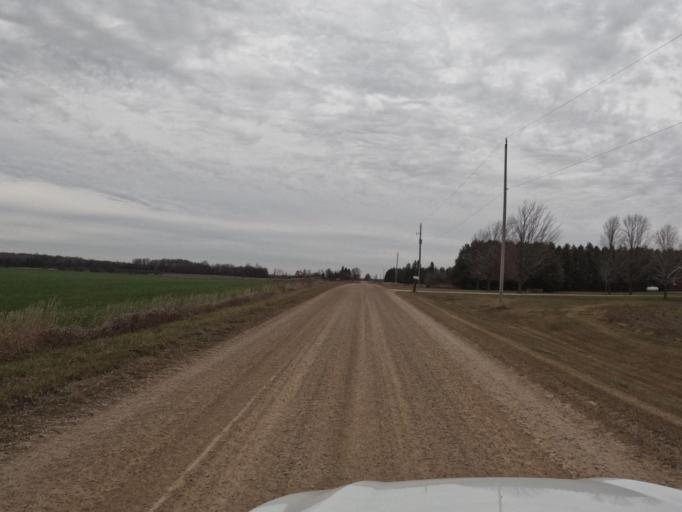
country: CA
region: Ontario
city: Shelburne
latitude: 44.0206
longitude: -80.3691
